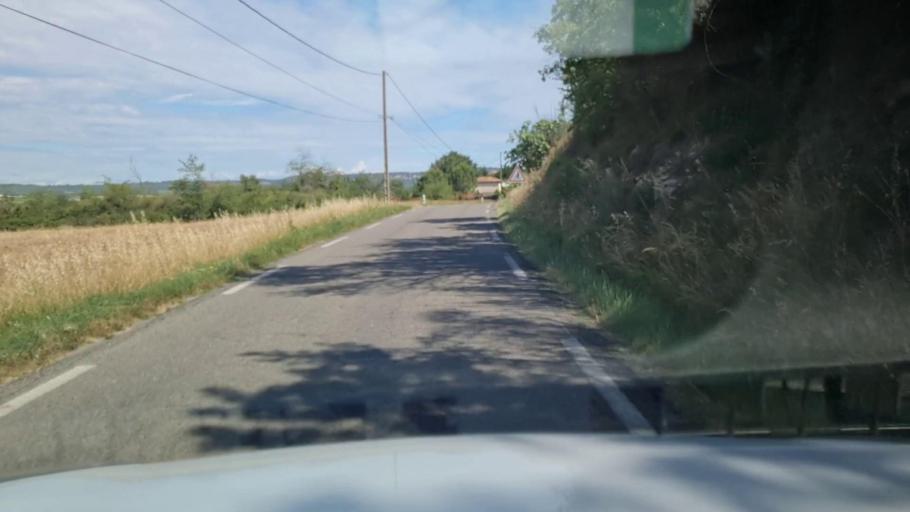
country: FR
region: Languedoc-Roussillon
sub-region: Departement du Gard
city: Nages-et-Solorgues
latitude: 43.7940
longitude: 4.2167
